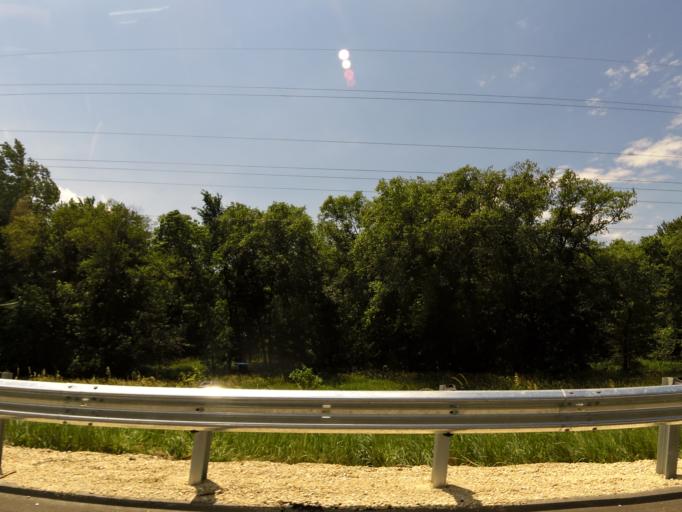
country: US
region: Iowa
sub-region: Bremer County
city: Tripoli
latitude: 42.7148
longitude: -92.1737
